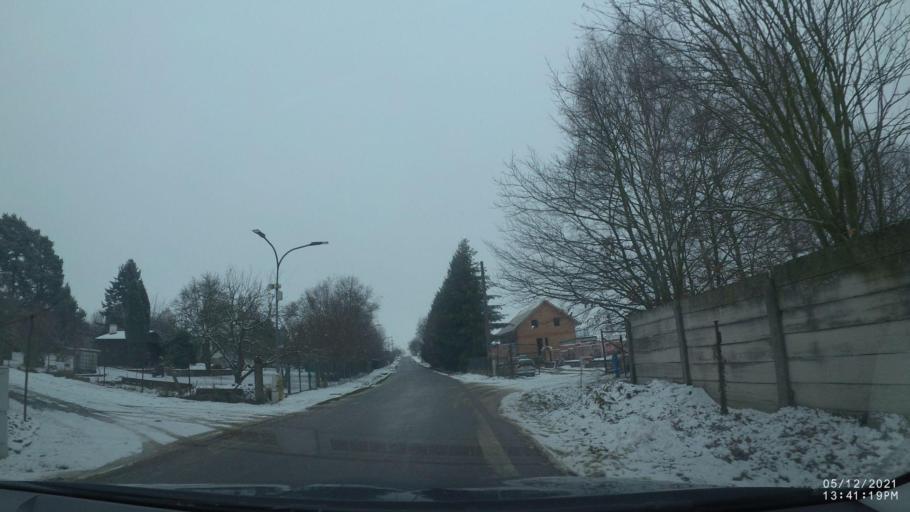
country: CZ
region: Kralovehradecky
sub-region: Okres Nachod
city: Police nad Metuji
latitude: 50.5326
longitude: 16.2403
